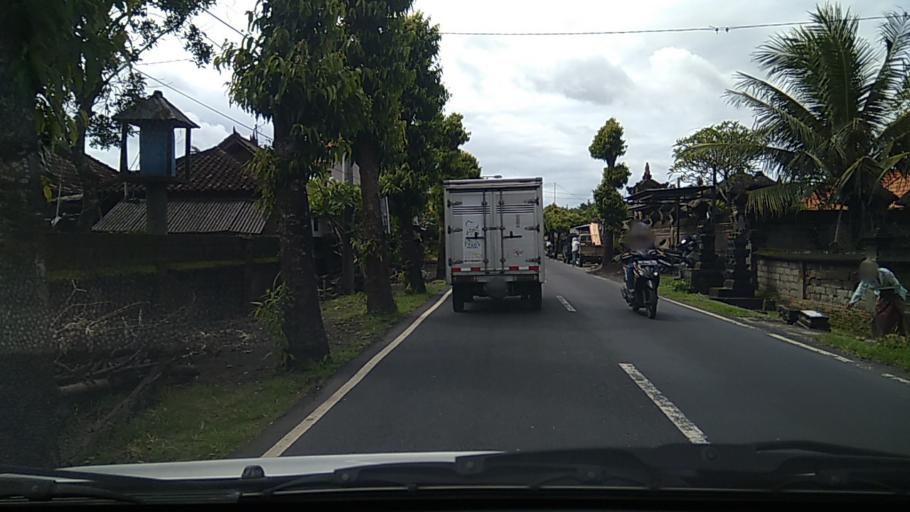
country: ID
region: Bali
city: Banjar Desa
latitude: -8.5878
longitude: 115.2541
